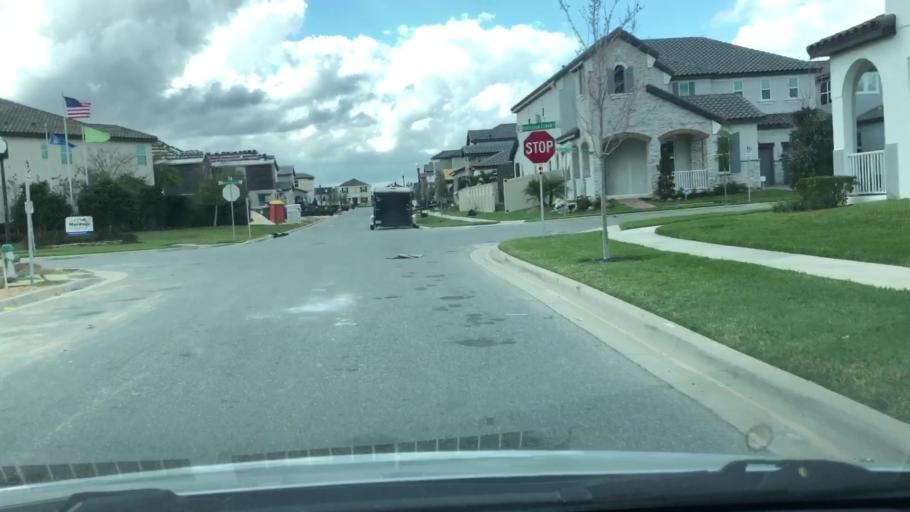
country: US
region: Florida
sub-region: Polk County
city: Citrus Ridge
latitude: 28.4318
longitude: -81.6214
